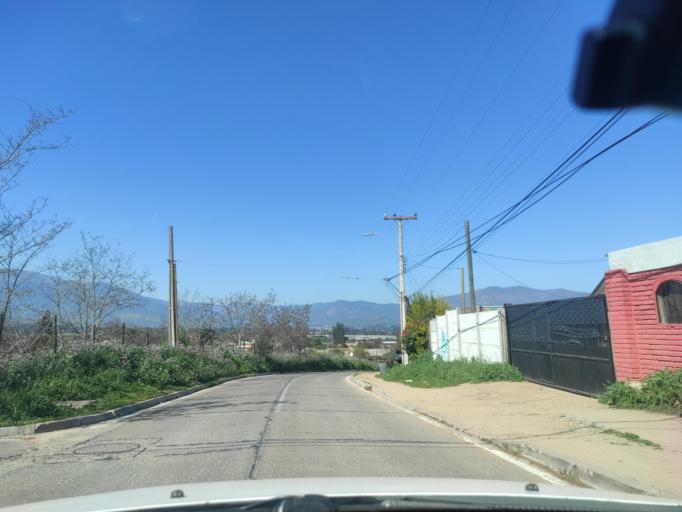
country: CL
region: Valparaiso
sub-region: Provincia de Marga Marga
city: Limache
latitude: -32.9932
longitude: -71.2257
